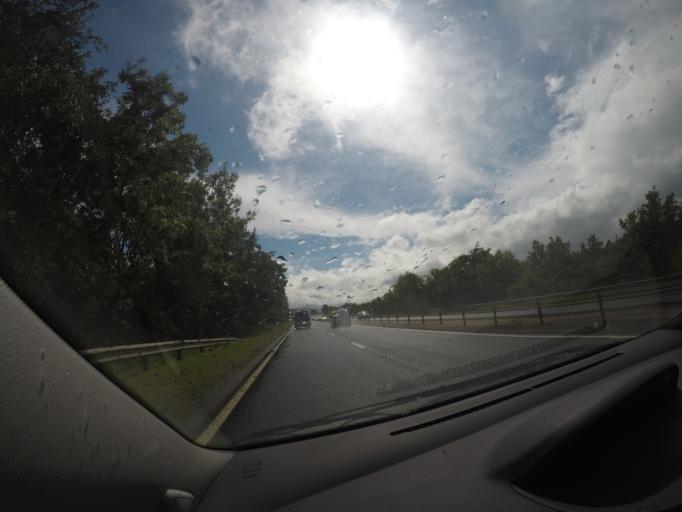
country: GB
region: Scotland
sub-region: Perth and Kinross
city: Auchterarder
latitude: 56.3109
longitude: -3.6615
